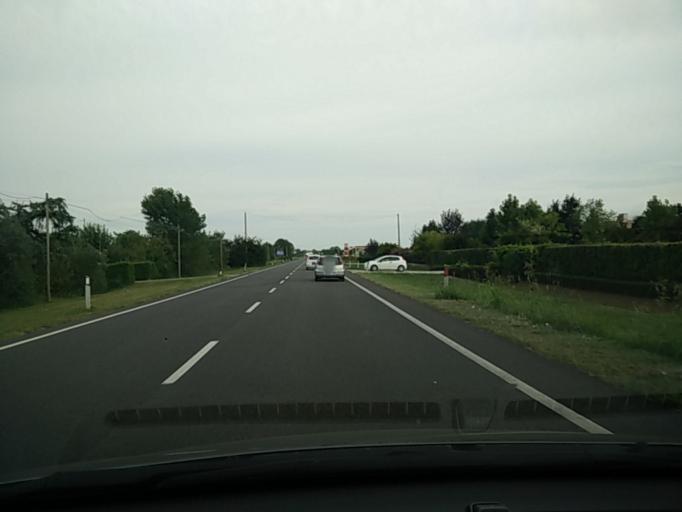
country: IT
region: Veneto
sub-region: Provincia di Venezia
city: Meolo
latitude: 45.6248
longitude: 12.4699
